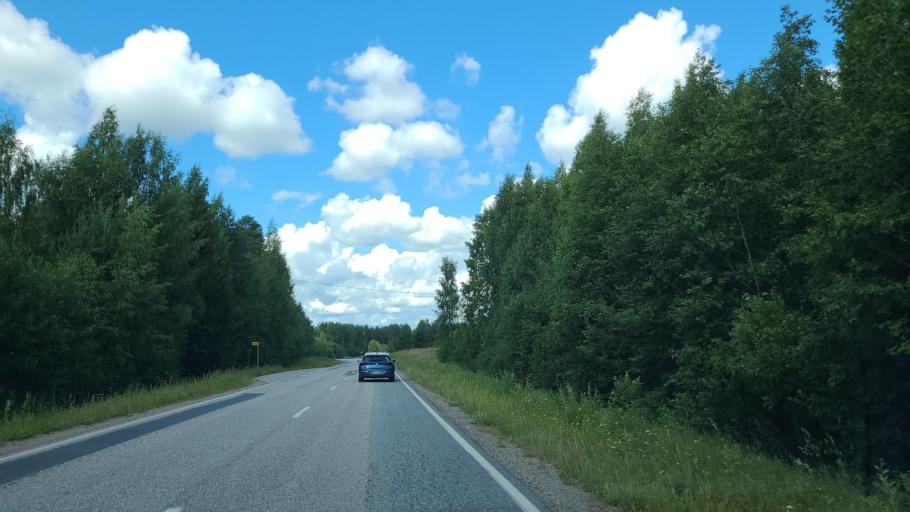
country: FI
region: Northern Savo
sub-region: Koillis-Savo
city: Kaavi
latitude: 62.9089
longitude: 28.7147
